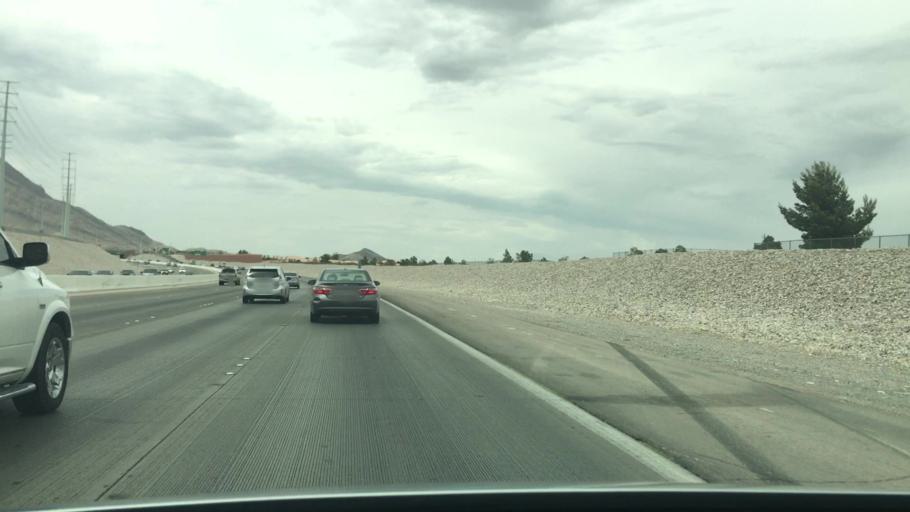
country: US
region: Nevada
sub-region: Clark County
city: Summerlin South
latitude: 36.1712
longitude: -115.3376
